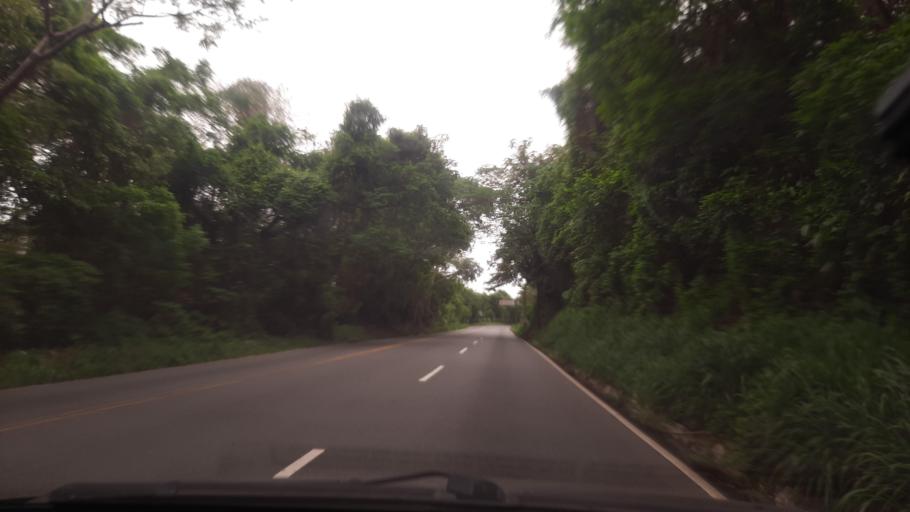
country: GT
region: Izabal
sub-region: Municipio de Los Amates
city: Los Amates
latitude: 15.2474
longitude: -89.1318
